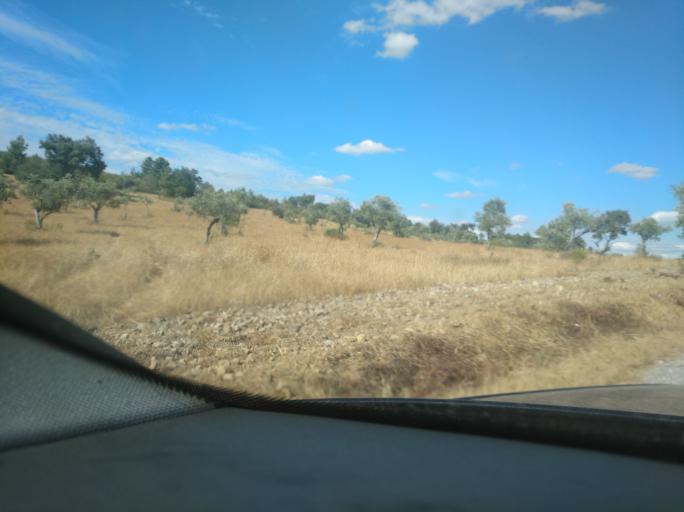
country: ES
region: Extremadura
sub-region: Provincia de Badajoz
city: La Codosera
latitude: 39.1484
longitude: -7.1699
